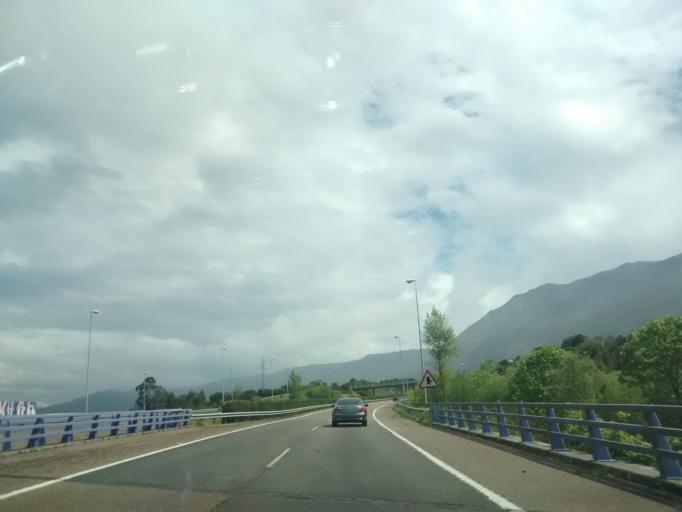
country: ES
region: Asturias
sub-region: Province of Asturias
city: Colunga
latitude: 43.4799
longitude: -5.2549
